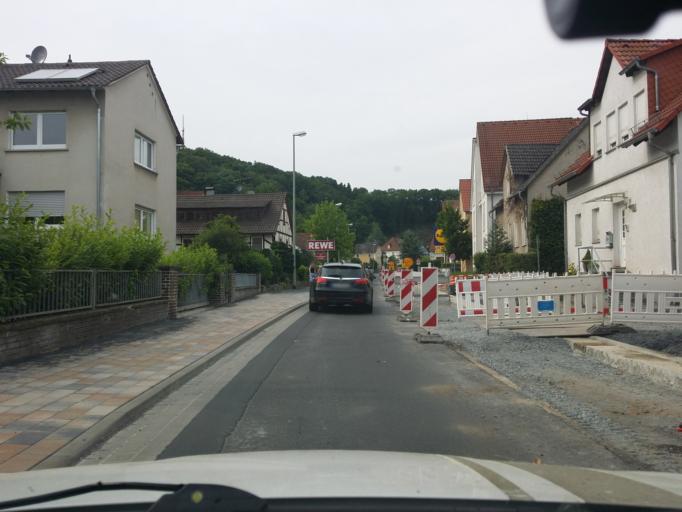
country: DE
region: Hesse
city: Eppstein
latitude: 50.1497
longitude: 8.3758
